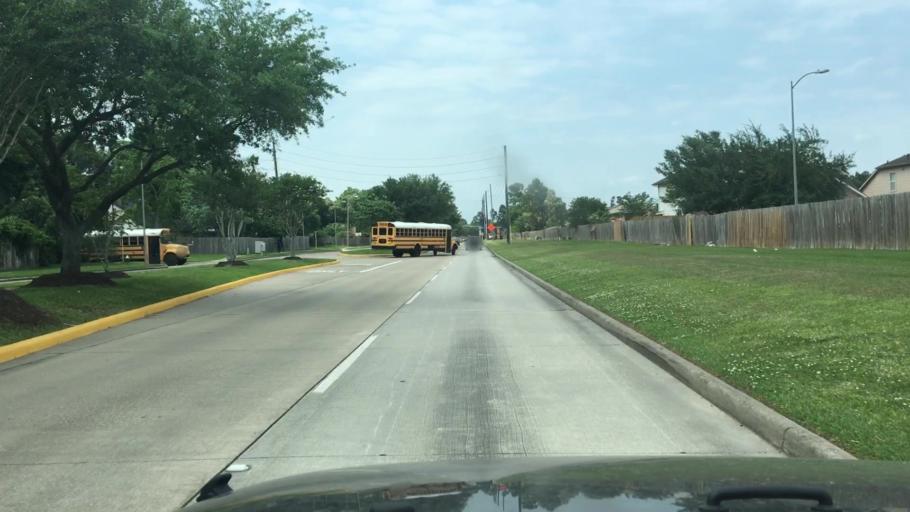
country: US
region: Texas
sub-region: Harris County
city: Atascocita
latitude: 29.9697
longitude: -95.2112
